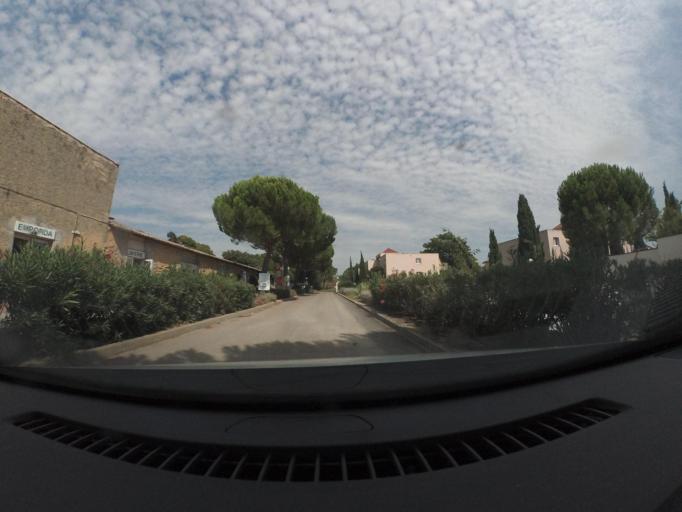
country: FR
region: Languedoc-Roussillon
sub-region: Departement de l'Herault
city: Baillargues
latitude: 43.6496
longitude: 4.0016
